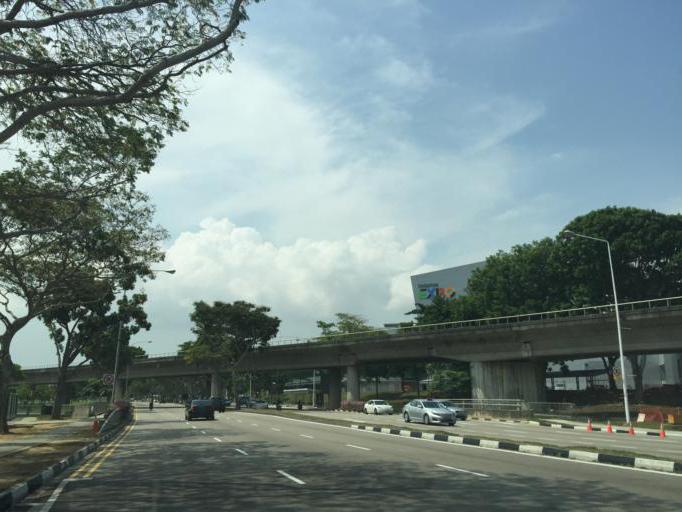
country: SG
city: Singapore
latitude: 1.3329
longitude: 103.9552
